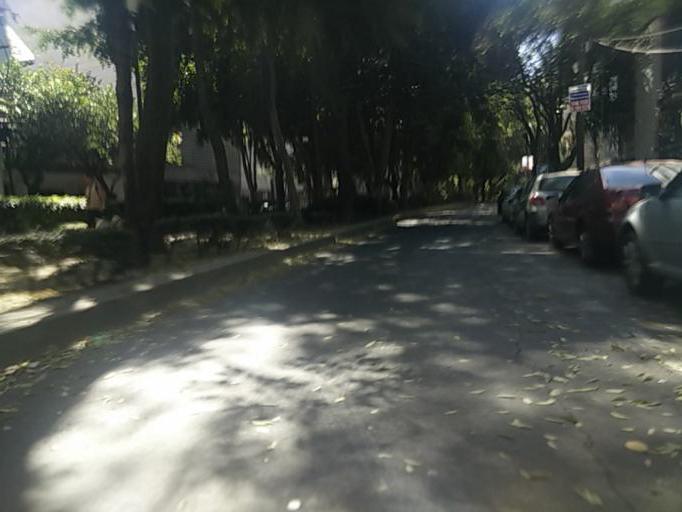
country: MX
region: Mexico City
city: Benito Juarez
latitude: 19.4108
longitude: -99.1679
